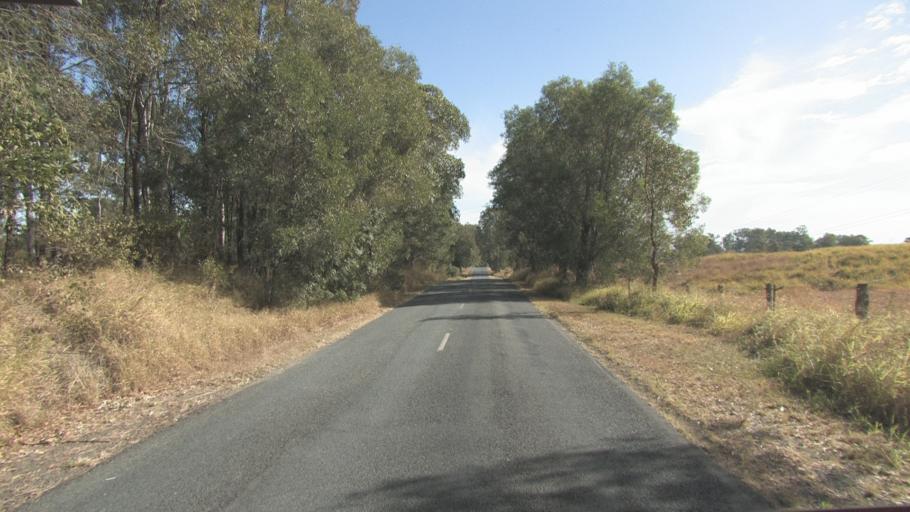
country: AU
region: Queensland
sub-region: Logan
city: Cedar Vale
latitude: -27.8673
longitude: 153.0146
